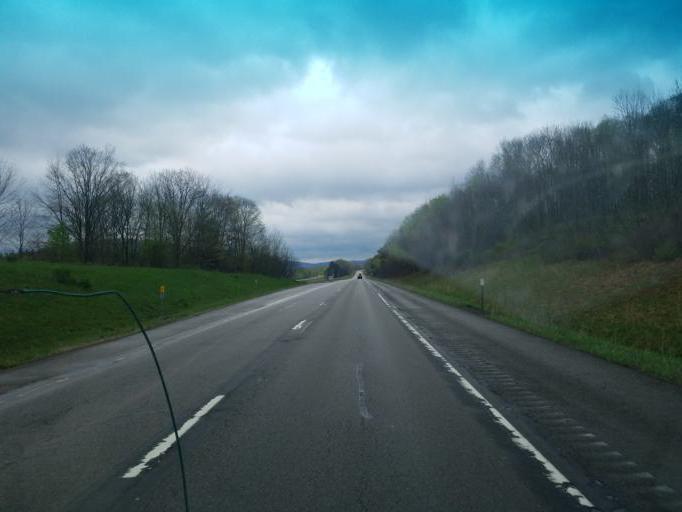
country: US
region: New York
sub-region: Cattaraugus County
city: Randolph
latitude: 42.1235
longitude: -78.9435
